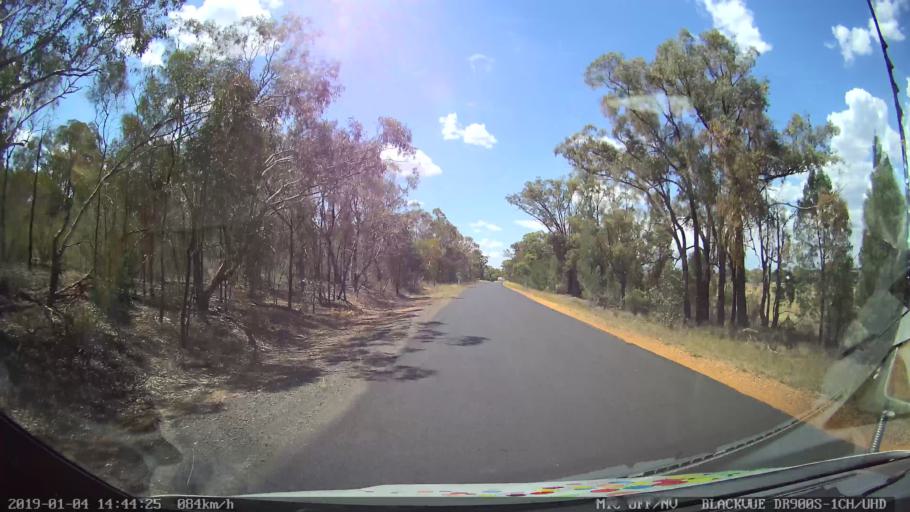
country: AU
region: New South Wales
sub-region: Dubbo Municipality
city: Dubbo
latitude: -32.1065
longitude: 148.6556
